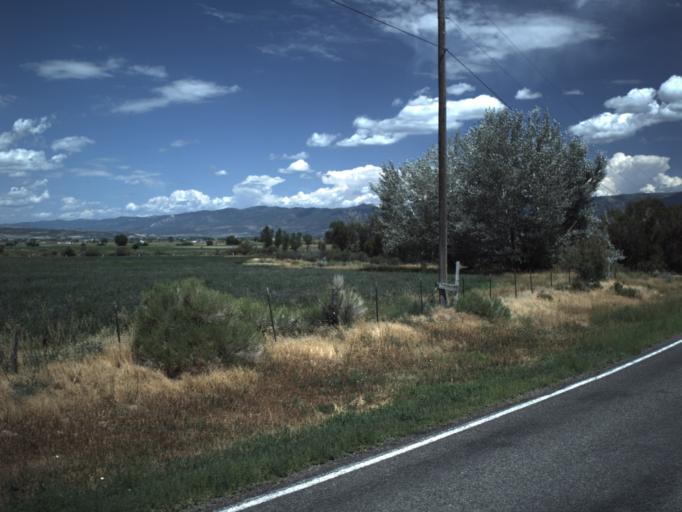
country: US
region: Utah
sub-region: Sanpete County
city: Mount Pleasant
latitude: 39.4811
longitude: -111.5139
